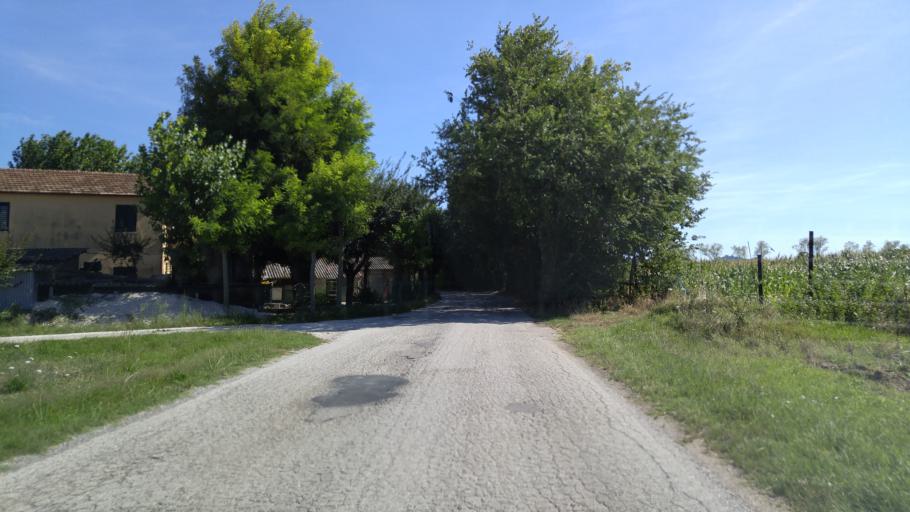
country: IT
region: The Marches
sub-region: Provincia di Pesaro e Urbino
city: Cuccurano
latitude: 43.7828
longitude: 12.9613
